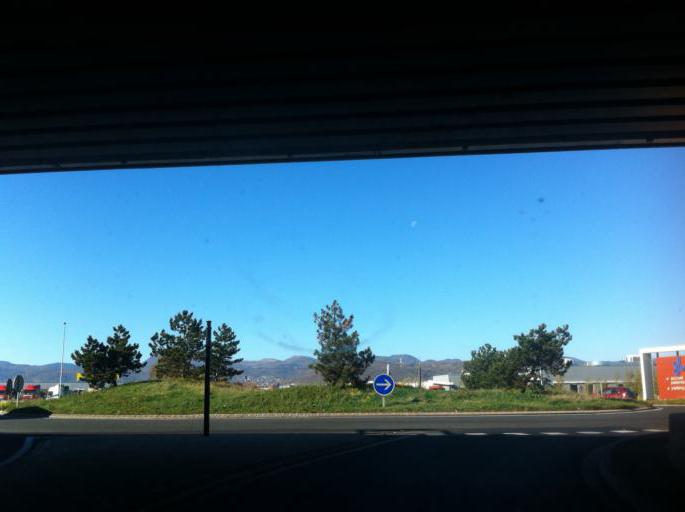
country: FR
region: Auvergne
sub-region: Departement du Puy-de-Dome
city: Aulnat
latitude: 45.7965
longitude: 3.1598
